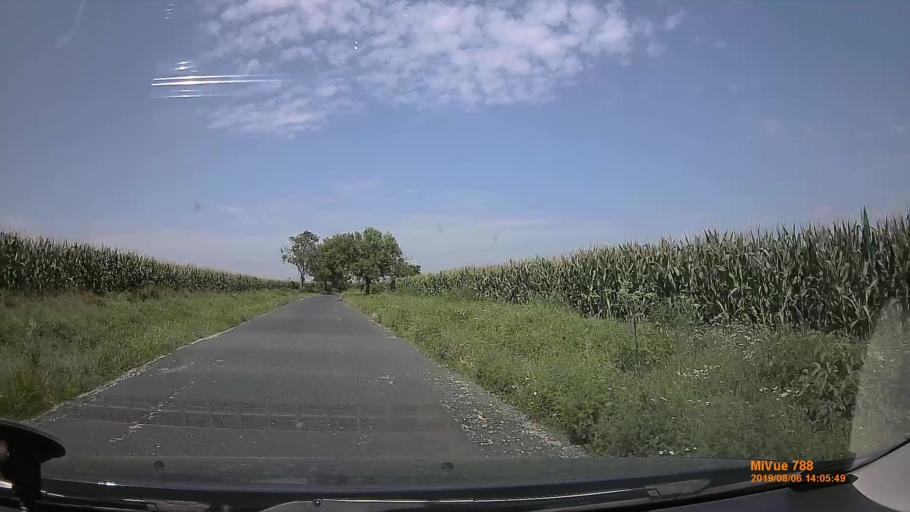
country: HU
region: Zala
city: Zalakomar
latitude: 46.5155
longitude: 17.0840
